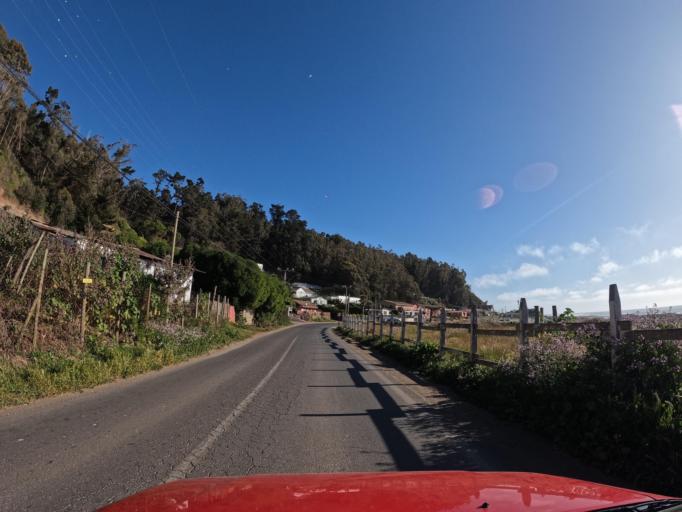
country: CL
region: Maule
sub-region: Provincia de Talca
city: Constitucion
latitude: -34.8882
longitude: -72.1716
